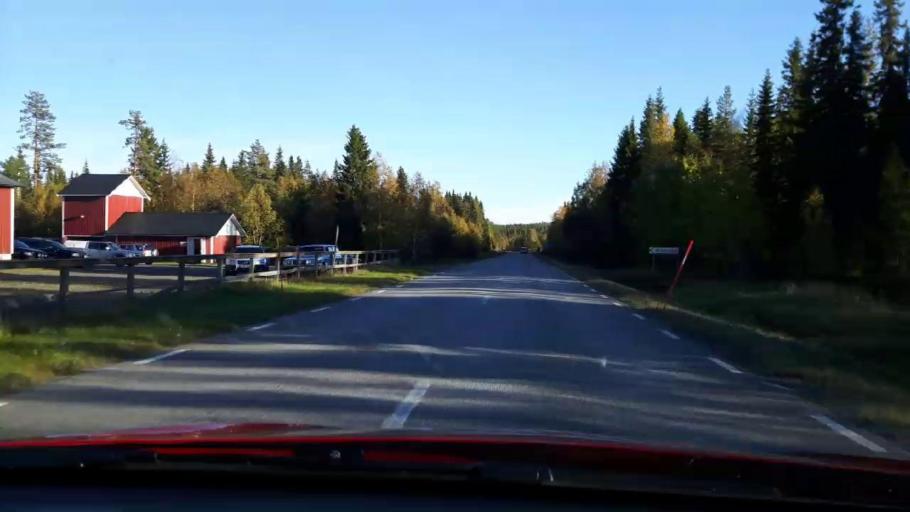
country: SE
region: Jaemtland
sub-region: OEstersunds Kommun
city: Lit
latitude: 63.7396
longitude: 14.7369
